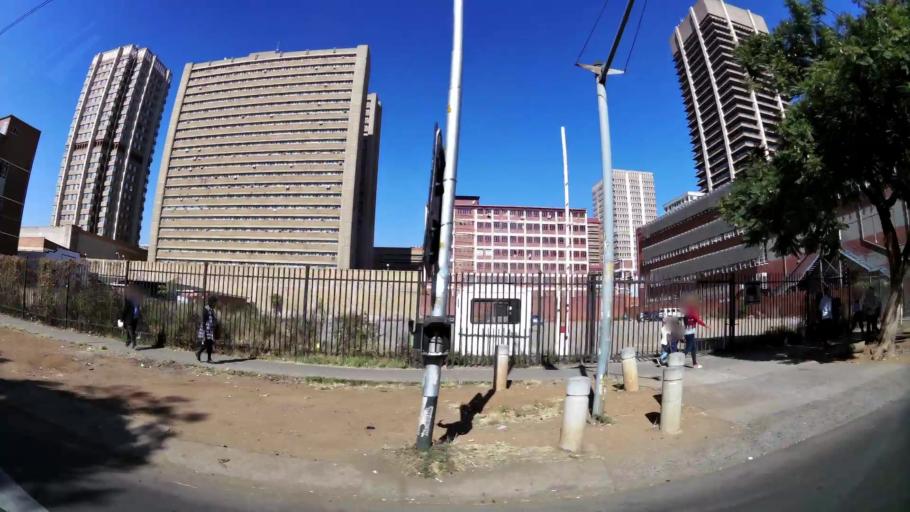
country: ZA
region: Gauteng
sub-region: City of Tshwane Metropolitan Municipality
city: Pretoria
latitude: -25.7433
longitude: 28.1910
